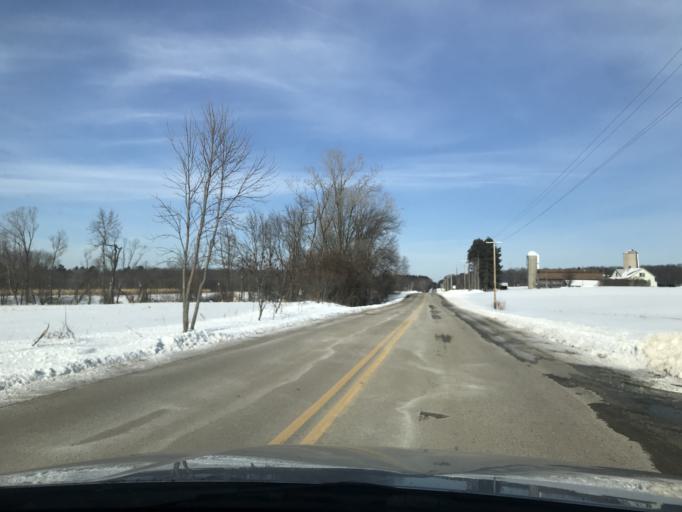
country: US
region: Wisconsin
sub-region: Oconto County
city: Oconto Falls
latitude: 45.1526
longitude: -88.1876
